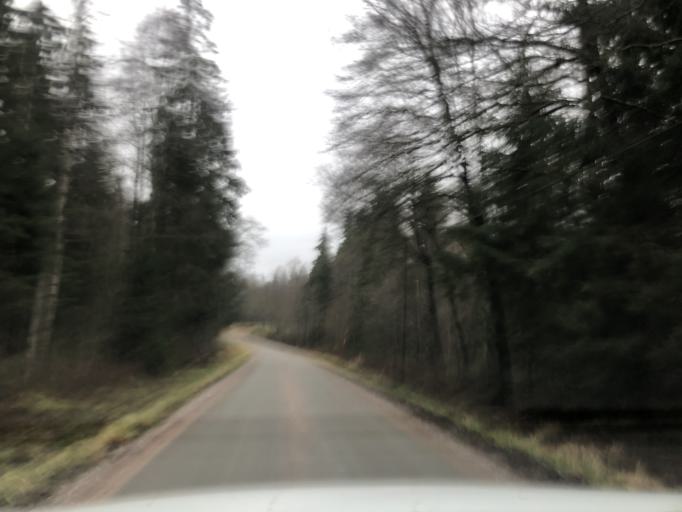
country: SE
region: Vaestra Goetaland
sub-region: Ulricehamns Kommun
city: Ulricehamn
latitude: 57.8613
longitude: 13.6034
